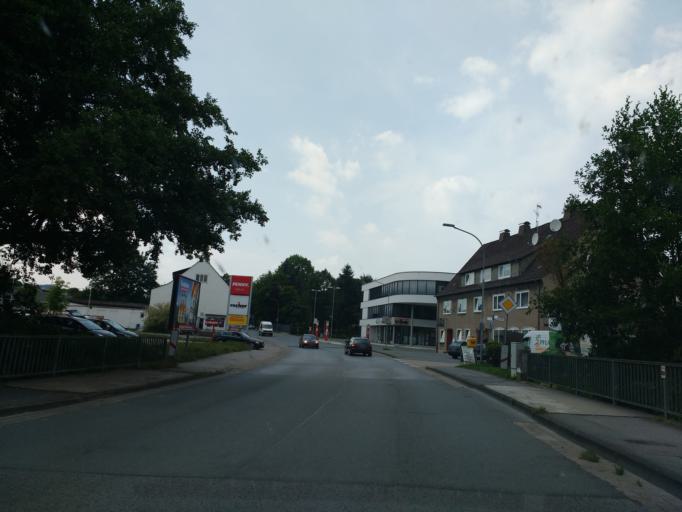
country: DE
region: North Rhine-Westphalia
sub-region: Regierungsbezirk Detmold
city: Barntrup
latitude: 52.0693
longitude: 9.1105
